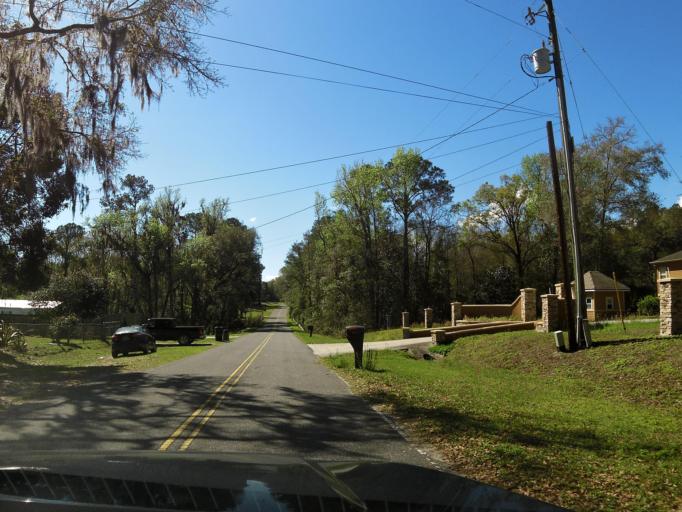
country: US
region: Florida
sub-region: Clay County
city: Green Cove Springs
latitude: 29.9821
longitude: -81.7060
